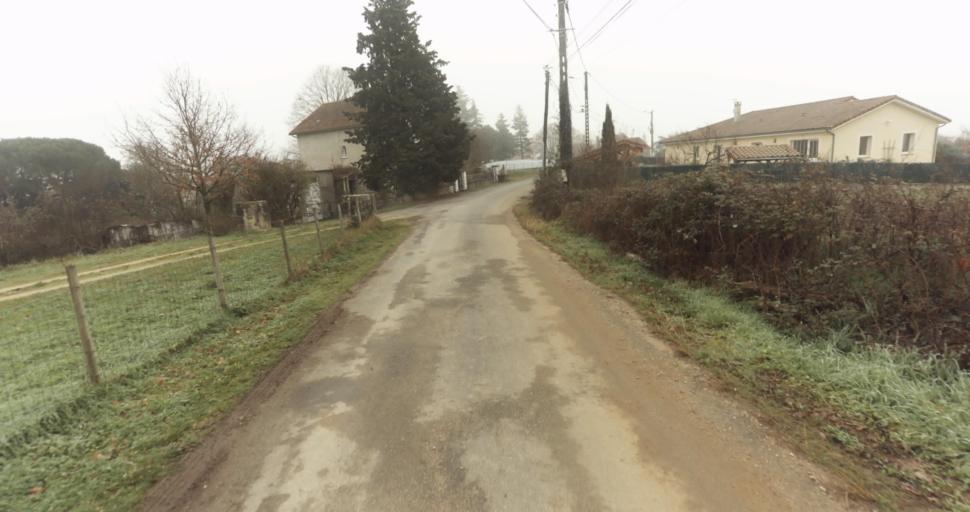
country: FR
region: Midi-Pyrenees
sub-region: Departement du Lot
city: Figeac
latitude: 44.6194
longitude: 2.0400
